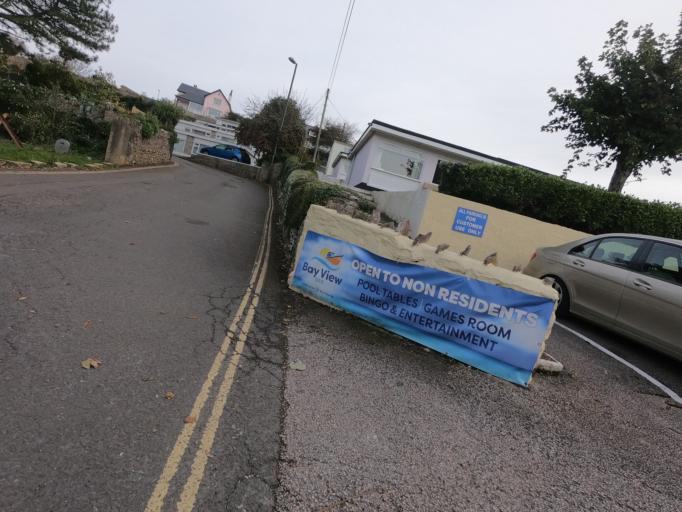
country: GB
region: England
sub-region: Borough of Torbay
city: Brixham
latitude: 50.4010
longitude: -3.5217
